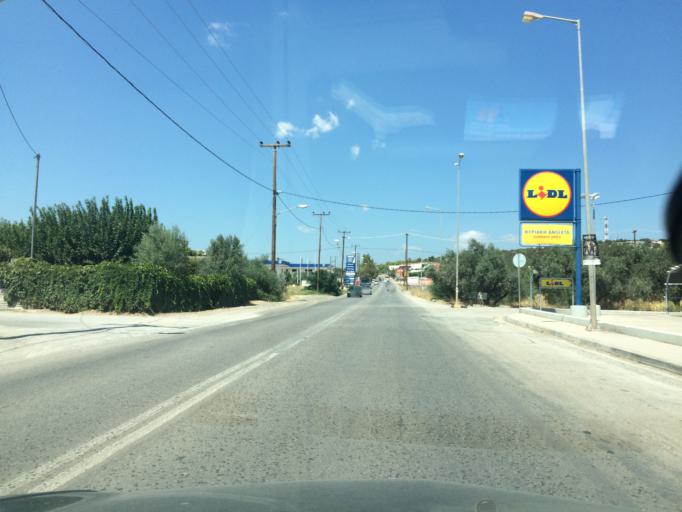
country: GR
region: Central Greece
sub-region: Nomos Evvoias
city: Nea Artaki
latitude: 38.5238
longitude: 23.6373
